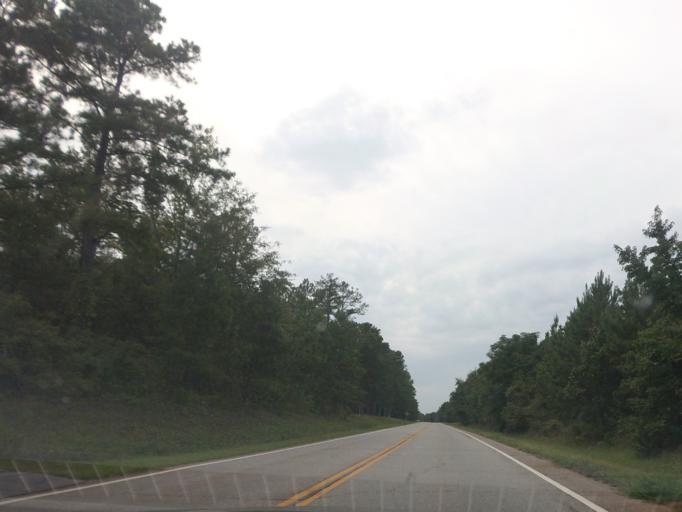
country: US
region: Georgia
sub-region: Twiggs County
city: Jeffersonville
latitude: 32.7100
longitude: -83.3829
